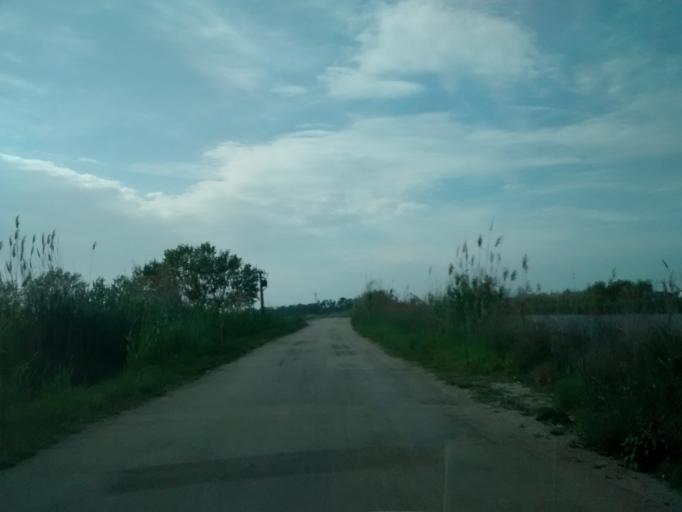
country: ES
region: Catalonia
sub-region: Provincia de Tarragona
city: Deltebre
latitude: 40.6942
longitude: 0.8392
